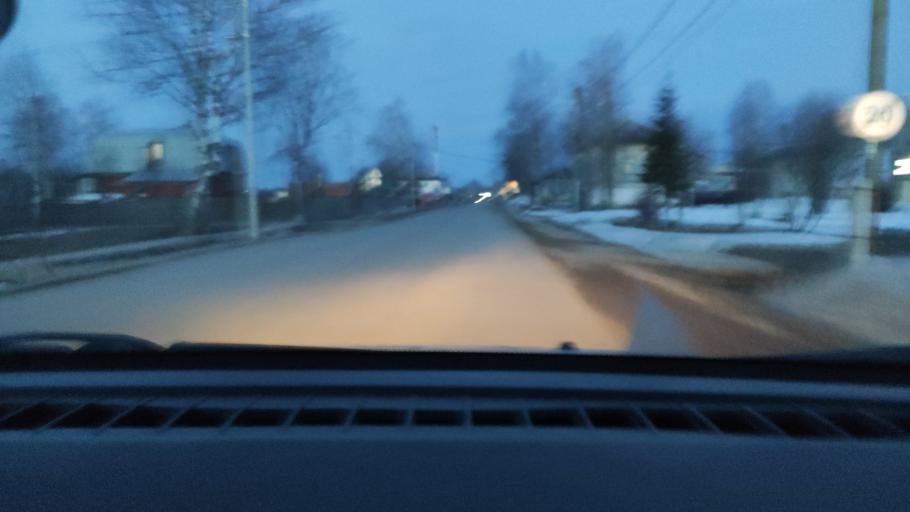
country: RU
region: Perm
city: Yug
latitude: 57.7328
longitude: 56.1723
